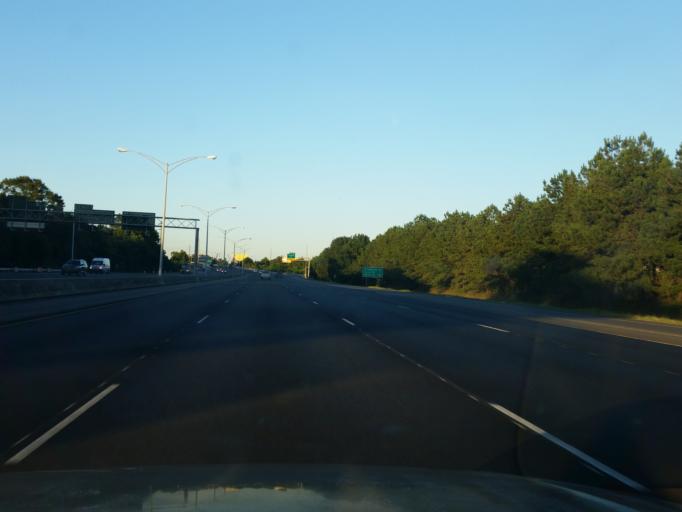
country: US
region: Alabama
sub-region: Mobile County
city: Mobile
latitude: 30.6628
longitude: -88.0553
